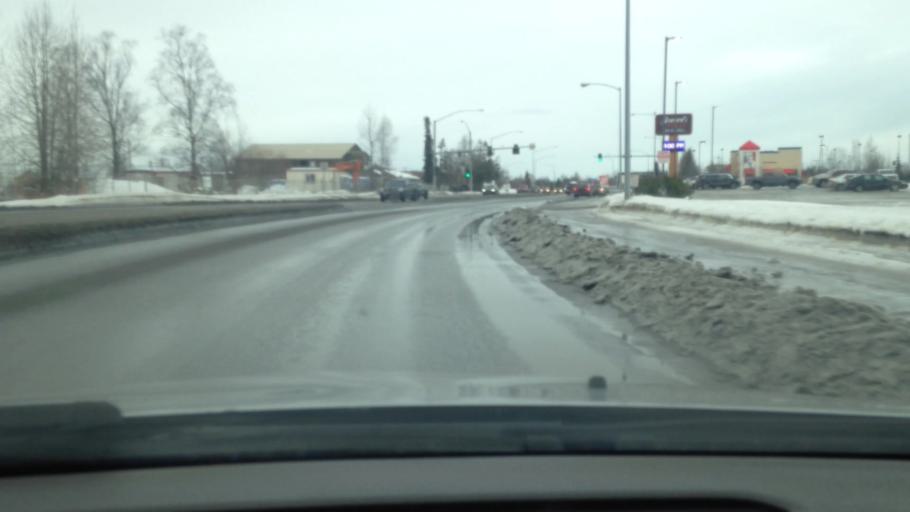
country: US
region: Alaska
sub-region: Anchorage Municipality
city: Anchorage
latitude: 61.1398
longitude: -149.8472
